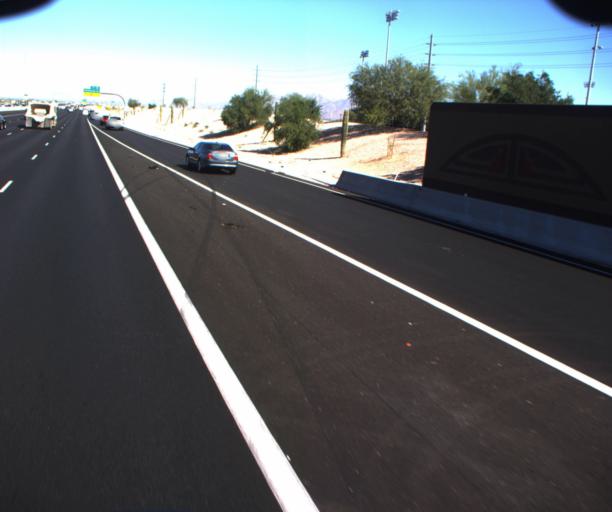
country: US
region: Arizona
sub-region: Maricopa County
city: Scottsdale
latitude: 33.5133
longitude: -111.8877
